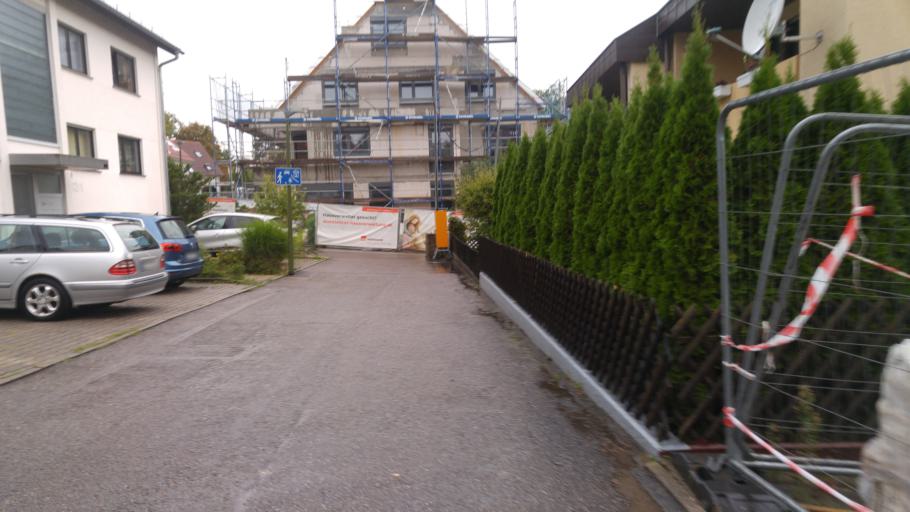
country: DE
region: Baden-Wuerttemberg
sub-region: Regierungsbezirk Stuttgart
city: Leonberg
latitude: 48.7995
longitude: 9.0068
